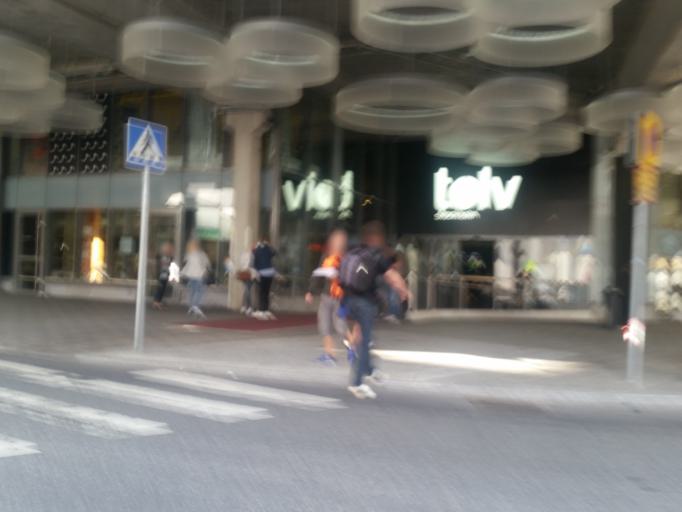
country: SE
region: Stockholm
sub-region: Stockholms Kommun
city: Arsta
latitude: 59.2917
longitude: 18.0827
